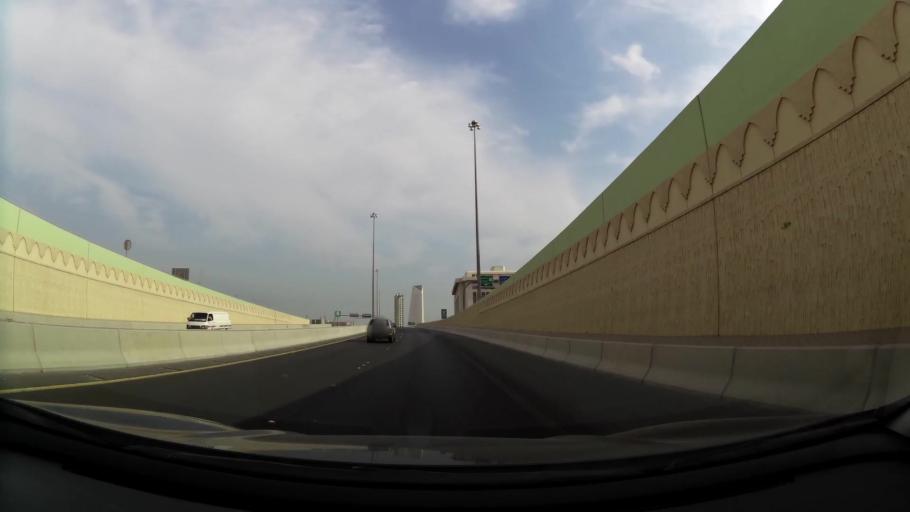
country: KW
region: Al Asimah
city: Kuwait City
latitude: 29.3680
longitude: 47.9650
